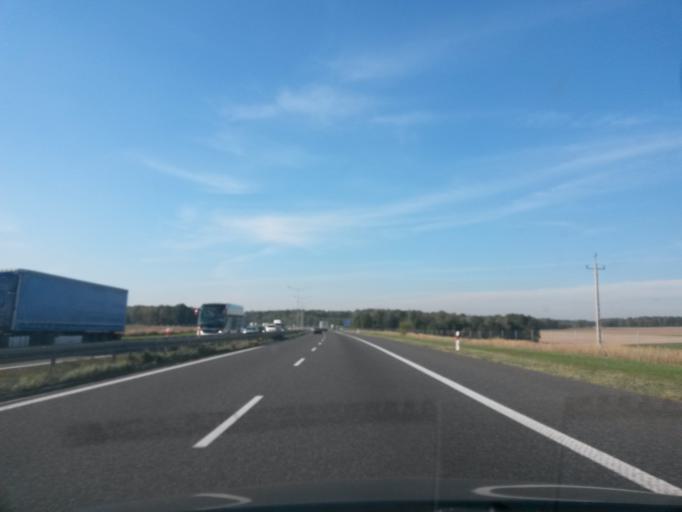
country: PL
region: Opole Voivodeship
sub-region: Powiat strzelecki
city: Ujazd
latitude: 50.4203
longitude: 18.3988
